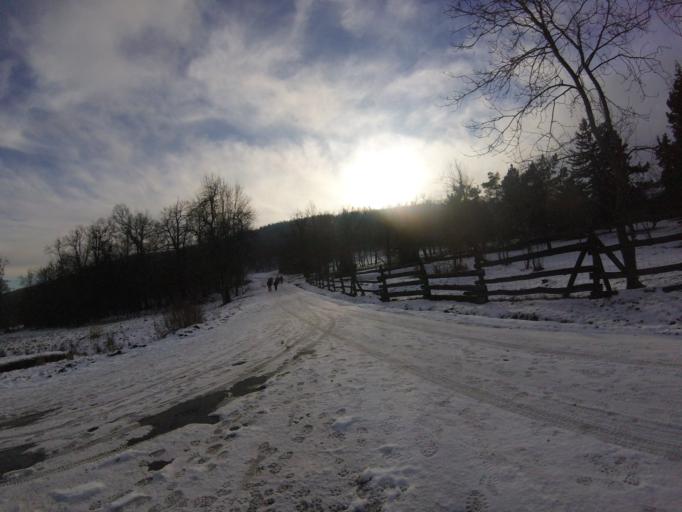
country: HU
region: Pest
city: Dunabogdany
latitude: 47.7384
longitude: 19.0124
